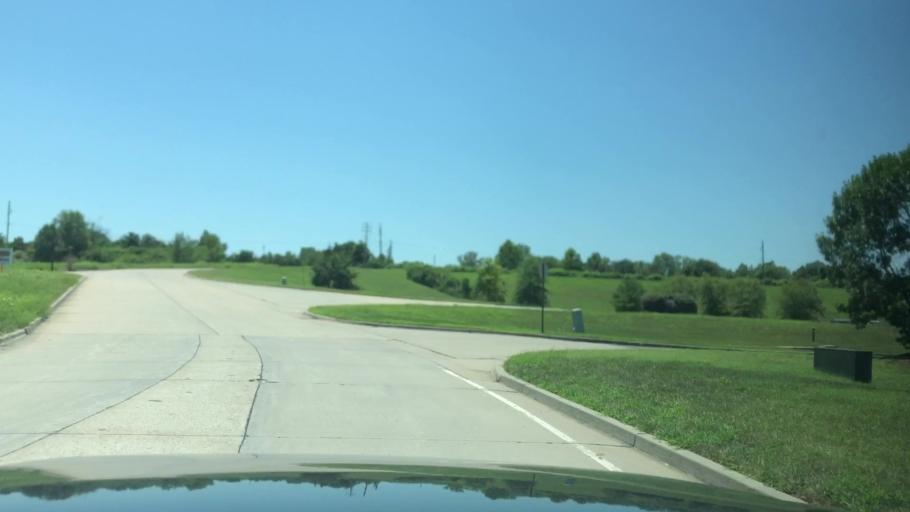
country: US
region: Illinois
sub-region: Saint Clair County
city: Alorton
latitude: 38.5551
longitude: -90.0786
